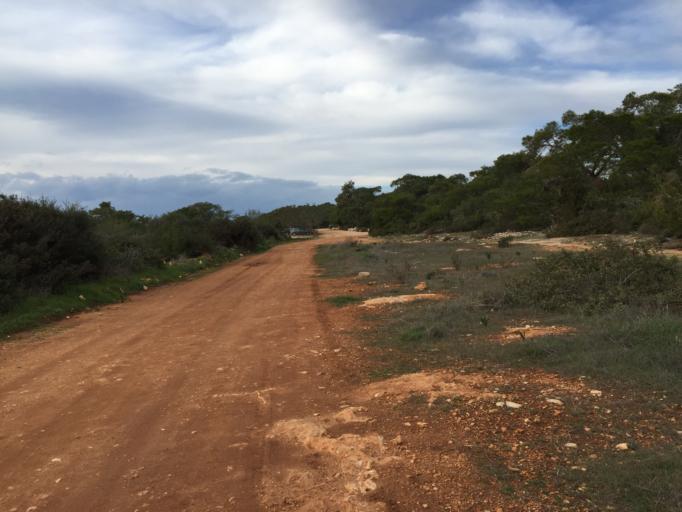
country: CY
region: Pafos
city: Pegeia
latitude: 34.8944
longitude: 32.3720
